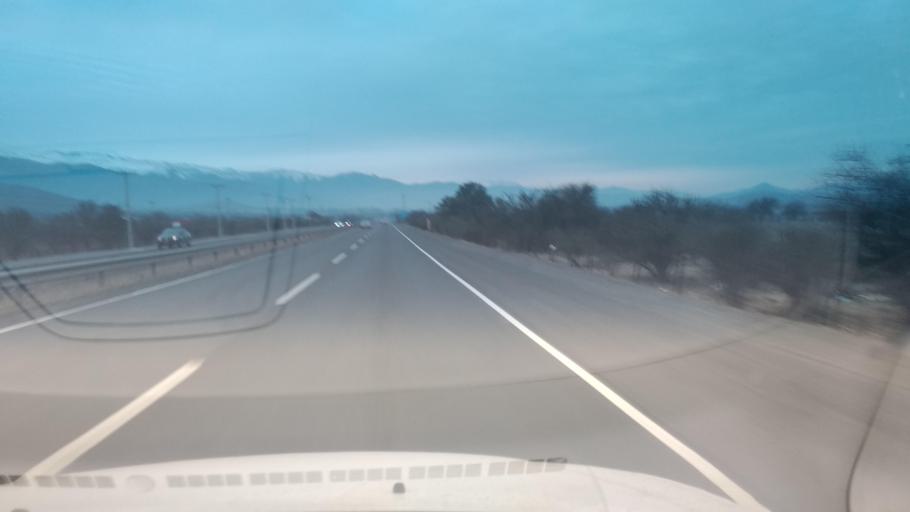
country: CL
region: Santiago Metropolitan
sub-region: Provincia de Chacabuco
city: Chicureo Abajo
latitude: -33.1162
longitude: -70.6828
